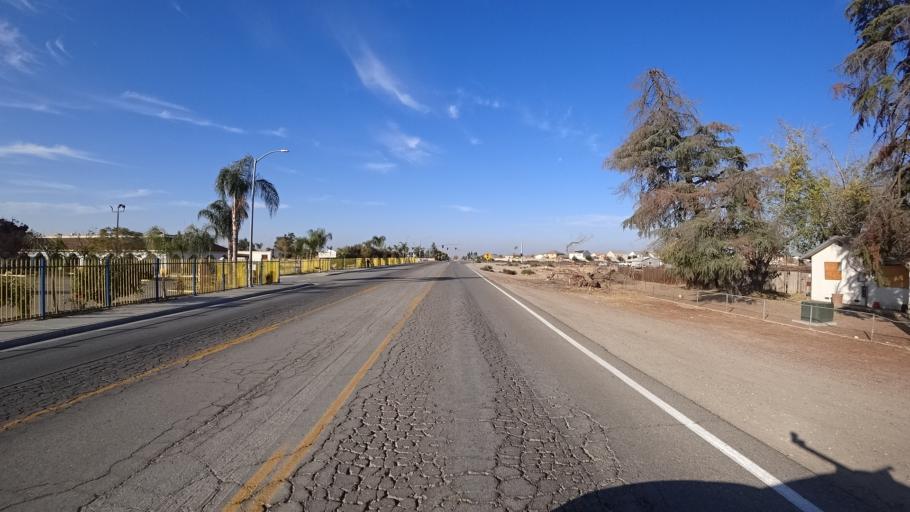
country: US
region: California
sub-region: Kern County
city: Greenfield
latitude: 35.2814
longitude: -119.0550
